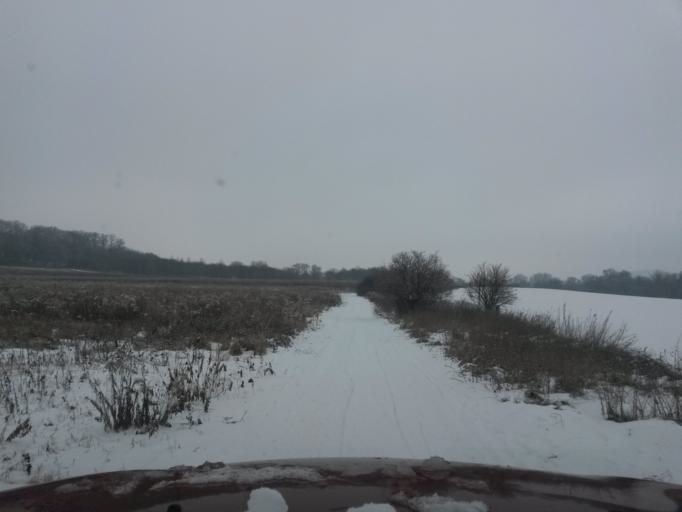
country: SK
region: Kosicky
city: Kosice
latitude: 48.7125
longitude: 21.3305
